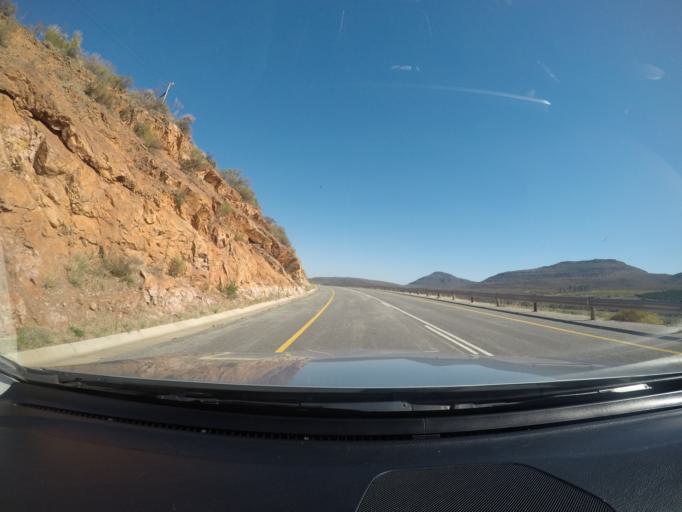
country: ZA
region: Western Cape
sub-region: West Coast District Municipality
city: Clanwilliam
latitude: -32.3938
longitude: 18.9499
